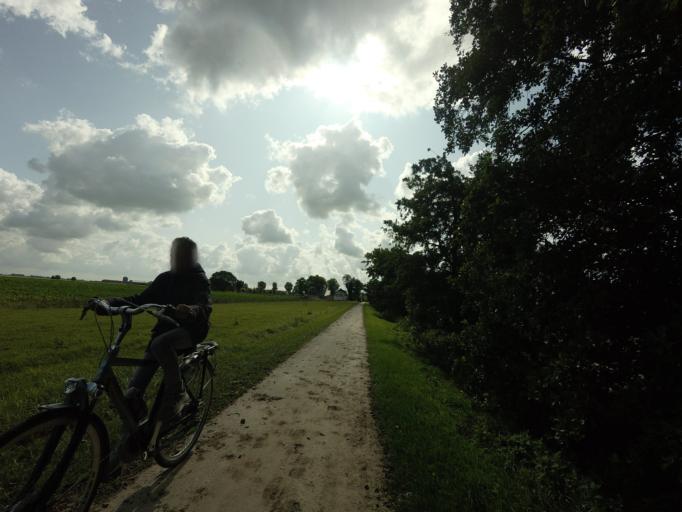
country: NL
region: Friesland
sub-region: Gemeente Het Bildt
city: Minnertsga
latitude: 53.2593
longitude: 5.5964
